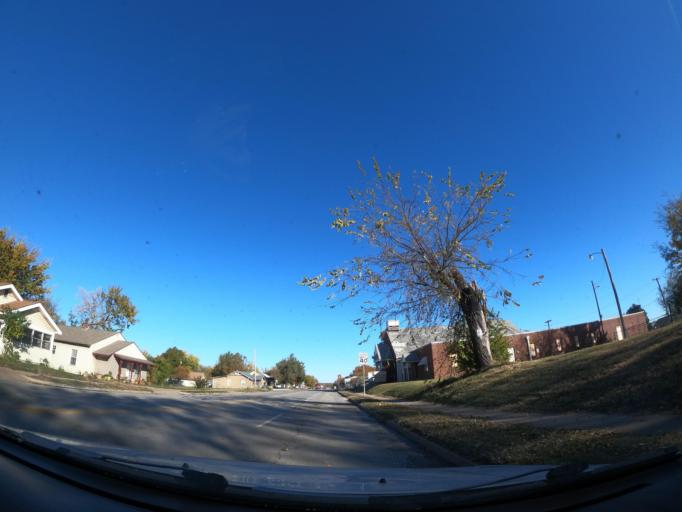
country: US
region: Oklahoma
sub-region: Tulsa County
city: Tulsa
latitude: 36.1662
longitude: -95.9671
